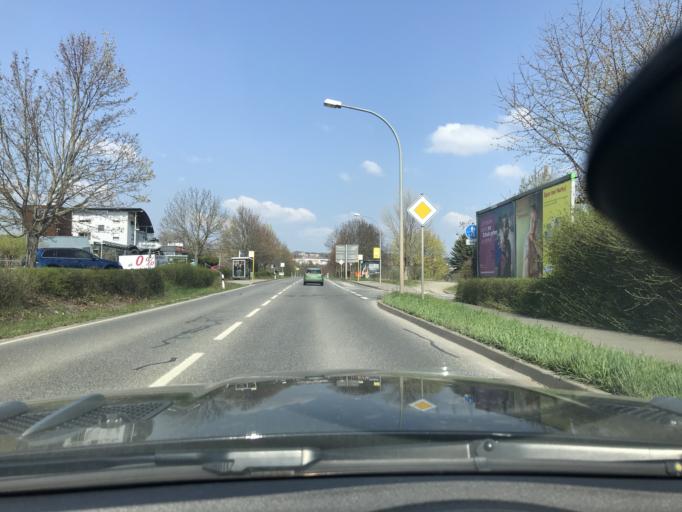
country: DE
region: Thuringia
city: Weimar
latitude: 51.0003
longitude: 11.3330
